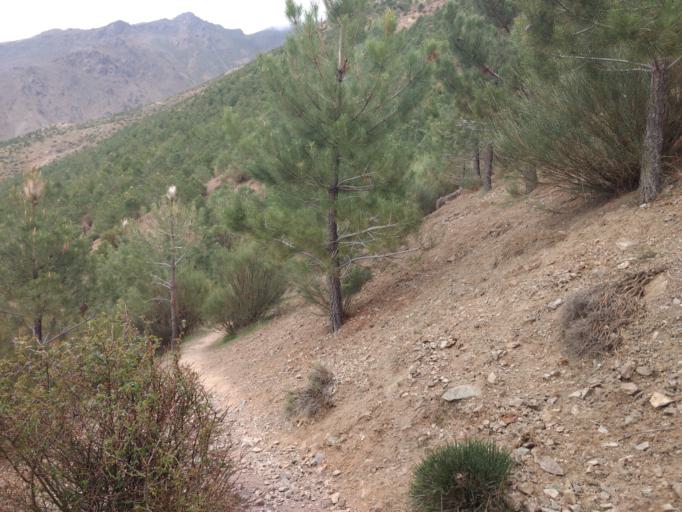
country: MA
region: Marrakech-Tensift-Al Haouz
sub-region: Al-Haouz
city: Moulay Brahim
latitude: 31.1334
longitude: -7.9074
